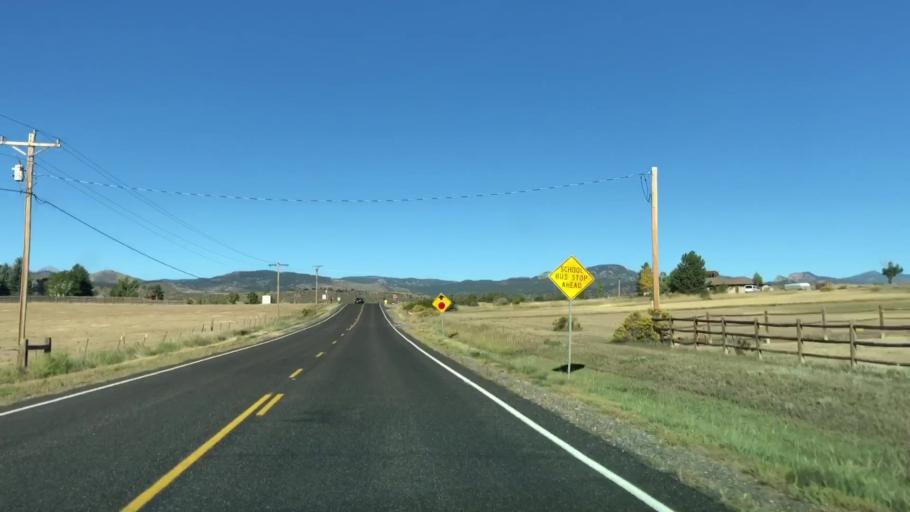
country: US
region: Colorado
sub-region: Larimer County
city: Loveland
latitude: 40.3785
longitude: -105.1607
